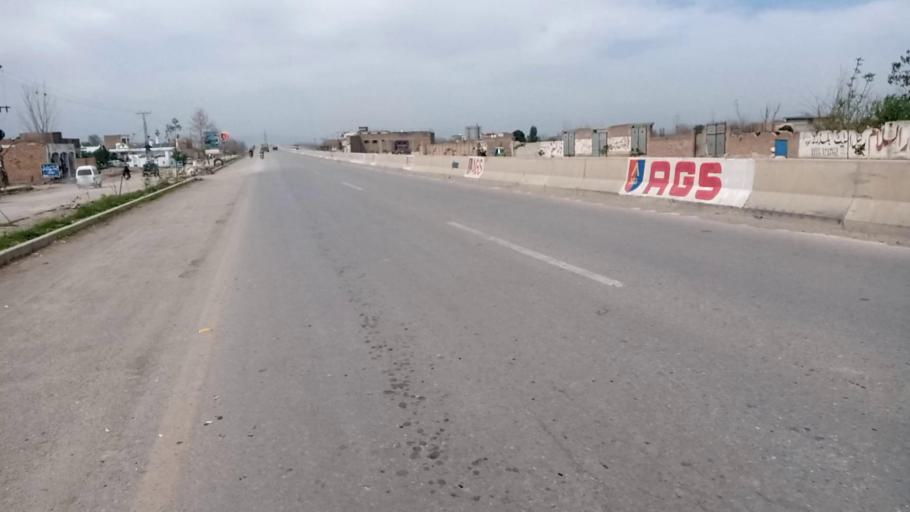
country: PK
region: Khyber Pakhtunkhwa
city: Peshawar
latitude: 34.0456
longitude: 71.6161
